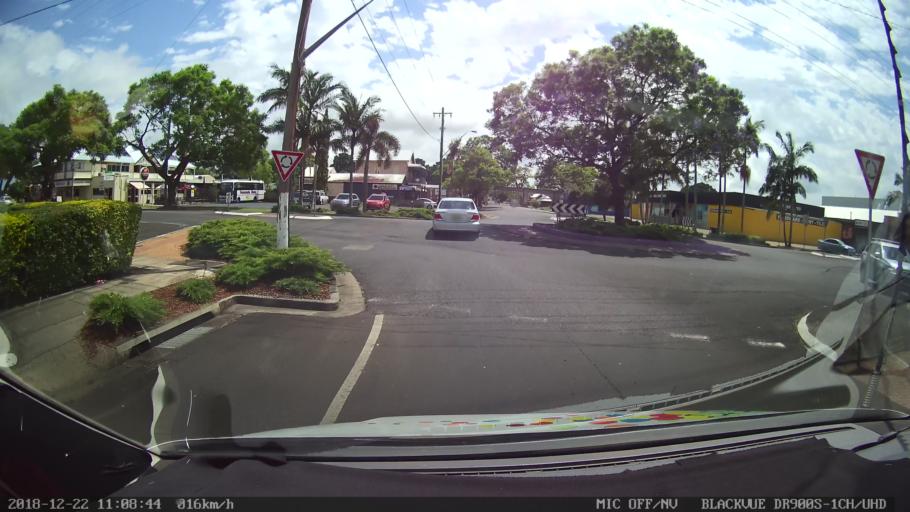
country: AU
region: New South Wales
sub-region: Clarence Valley
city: Grafton
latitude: -29.6883
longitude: 152.9321
